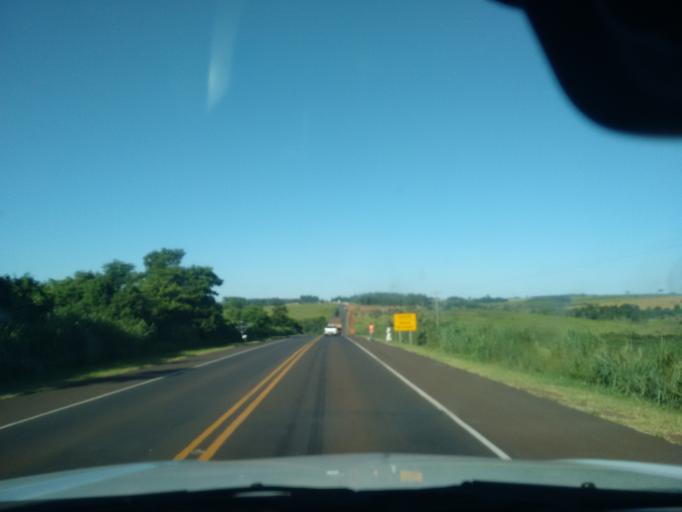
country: PY
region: Canindeyu
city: Salto del Guaira
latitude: -23.9688
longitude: -54.3287
